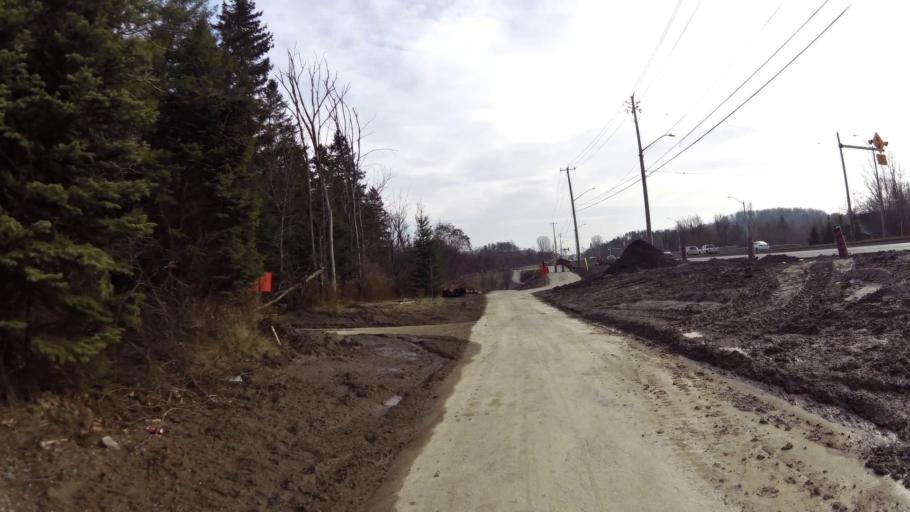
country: CA
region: Ontario
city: Kitchener
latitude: 43.3904
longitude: -80.4237
